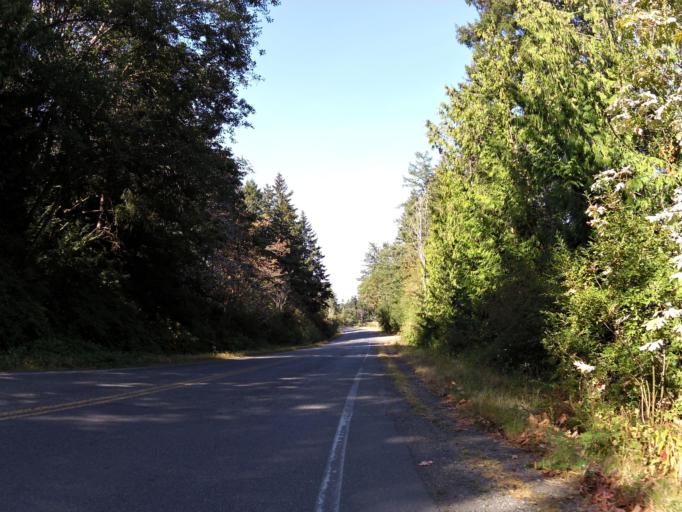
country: CA
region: British Columbia
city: North Saanich
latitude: 48.6260
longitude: -123.5280
